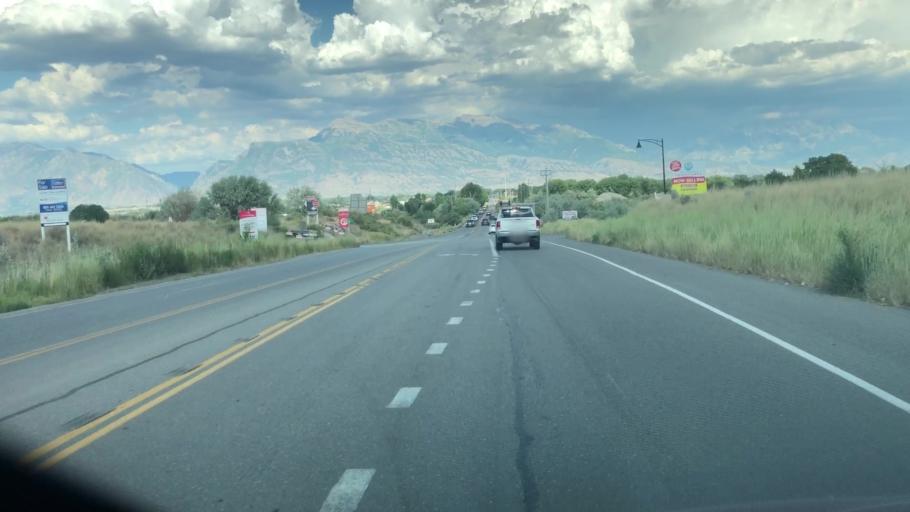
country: US
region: Utah
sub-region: Utah County
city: Saratoga Springs
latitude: 40.3874
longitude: -111.9081
